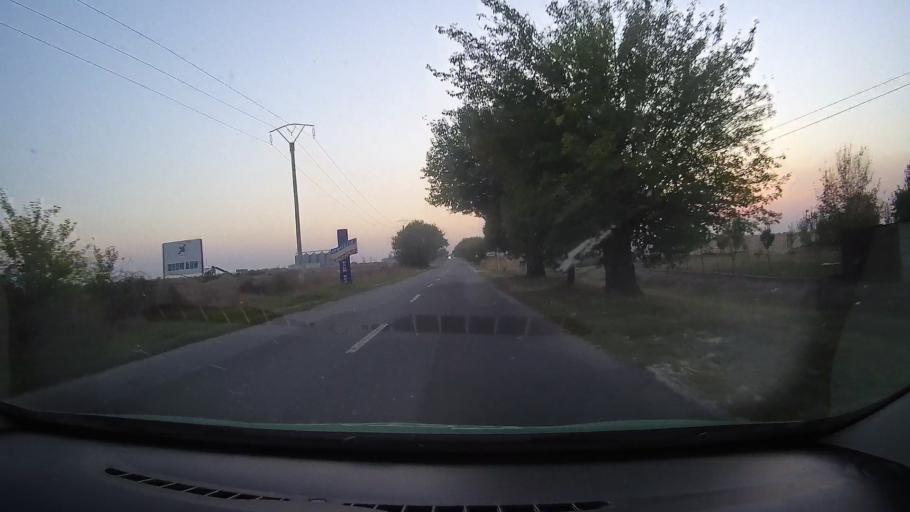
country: RO
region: Arad
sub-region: Comuna Santana
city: Santana
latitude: 46.3366
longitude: 21.4884
